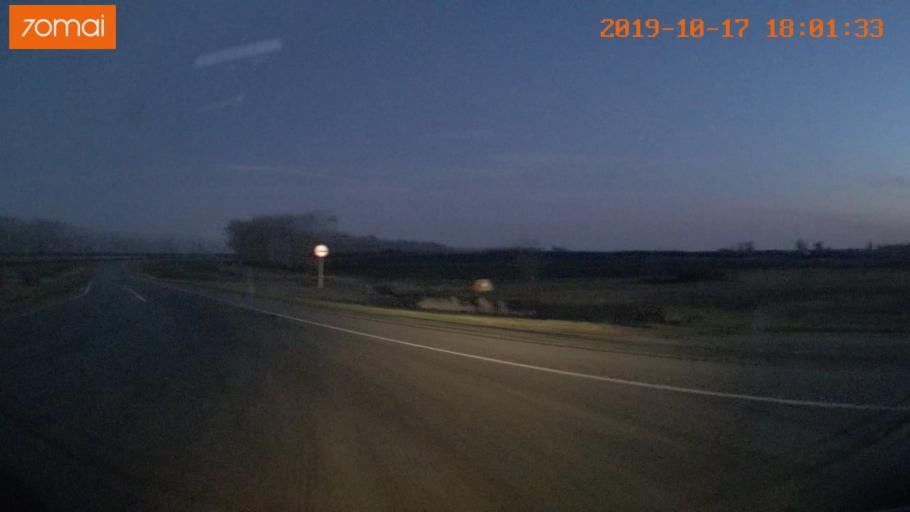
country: RU
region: Tula
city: Kurkino
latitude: 53.5076
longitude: 38.6101
